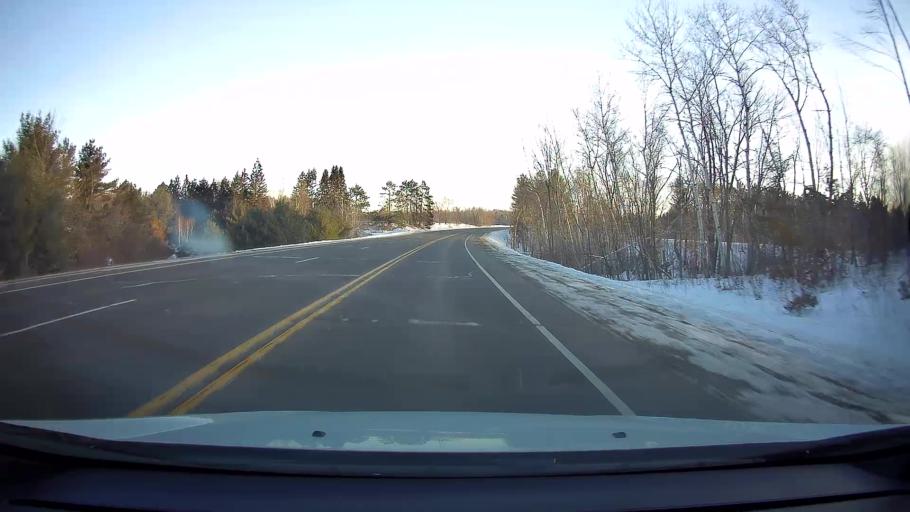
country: US
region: Wisconsin
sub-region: Barron County
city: Turtle Lake
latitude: 45.4610
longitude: -92.0996
